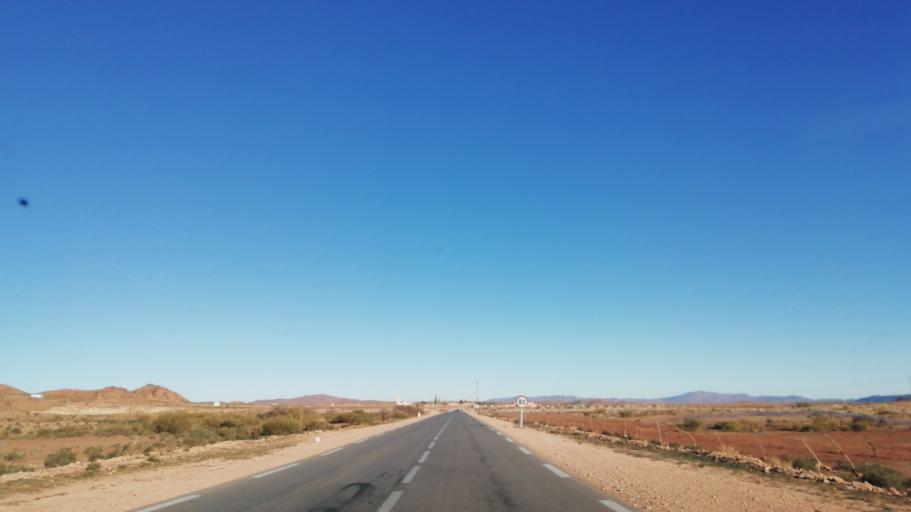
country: DZ
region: El Bayadh
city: El Abiodh Sidi Cheikh
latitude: 33.1614
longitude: 0.3544
